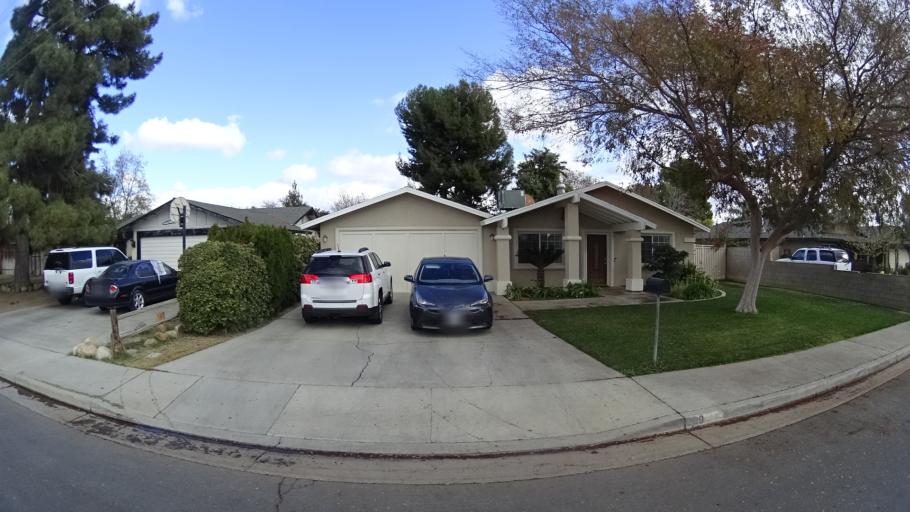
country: US
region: California
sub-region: Kern County
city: Bakersfield
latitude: 35.3559
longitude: -118.9453
